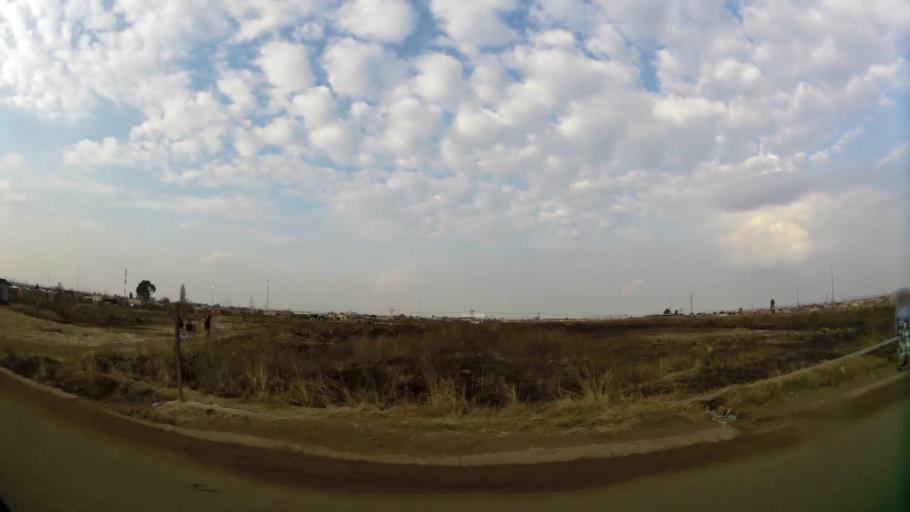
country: ZA
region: Gauteng
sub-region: Sedibeng District Municipality
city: Vanderbijlpark
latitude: -26.6711
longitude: 27.8680
